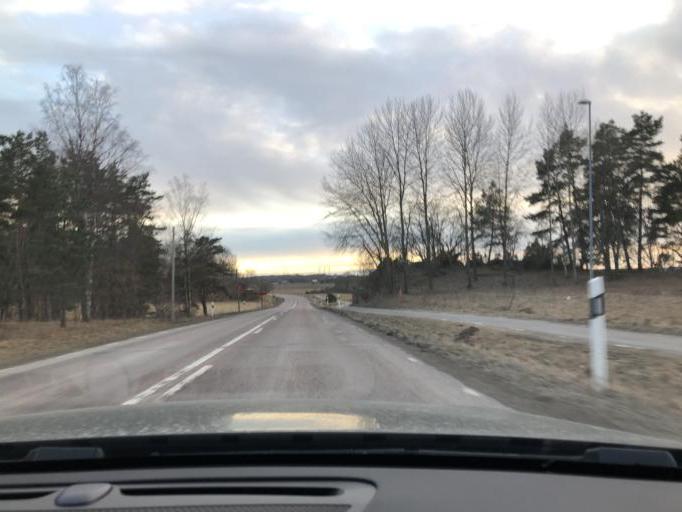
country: SE
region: Uppsala
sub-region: Uppsala Kommun
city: Gamla Uppsala
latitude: 59.9340
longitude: 17.6443
